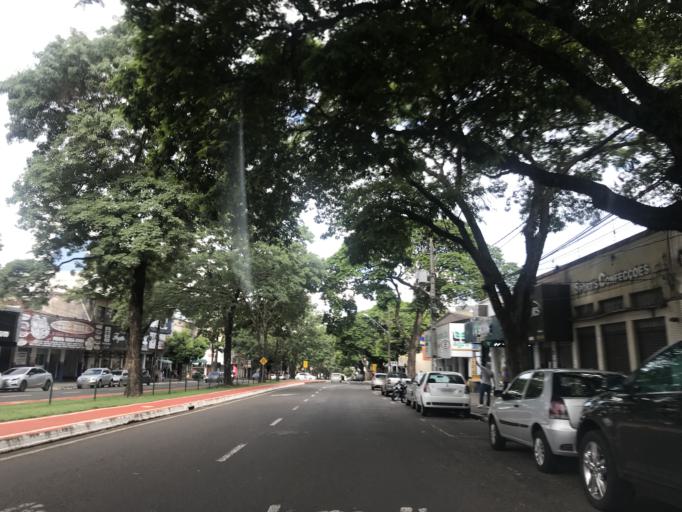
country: BR
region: Parana
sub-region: Maringa
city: Maringa
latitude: -23.4225
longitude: -51.9524
